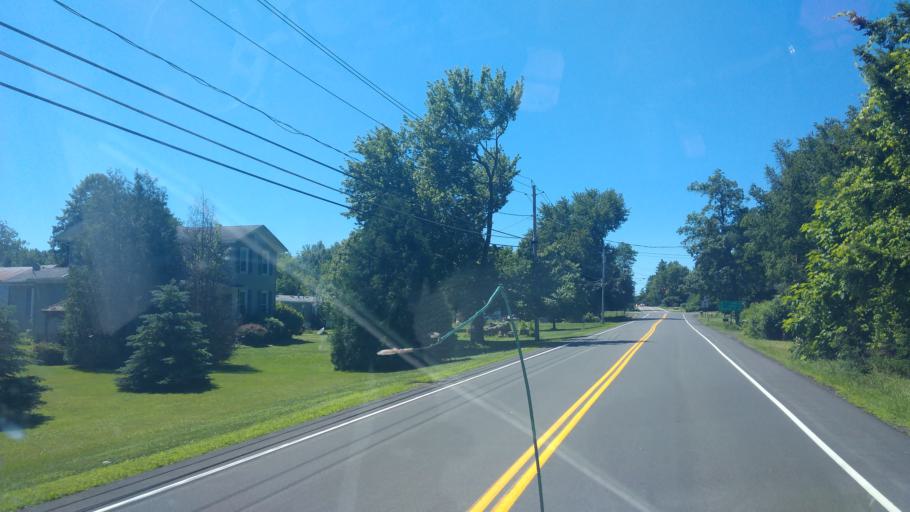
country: US
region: New York
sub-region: Wayne County
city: Sodus
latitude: 43.2080
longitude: -76.9816
